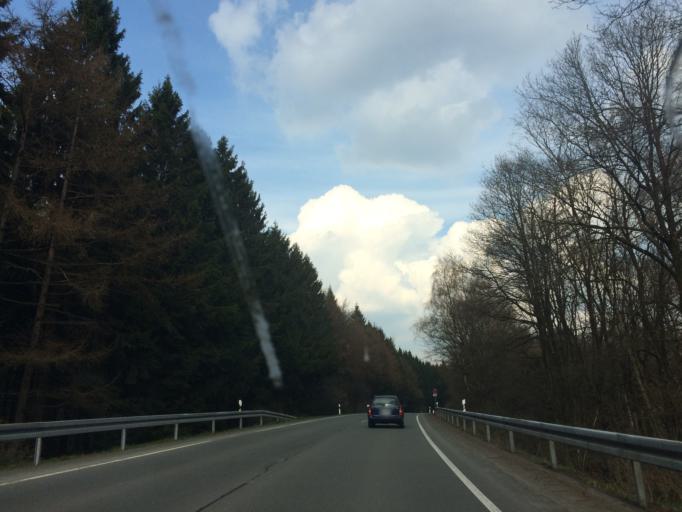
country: DE
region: North Rhine-Westphalia
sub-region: Regierungsbezirk Arnsberg
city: Luedenscheid
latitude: 51.2657
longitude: 7.6173
